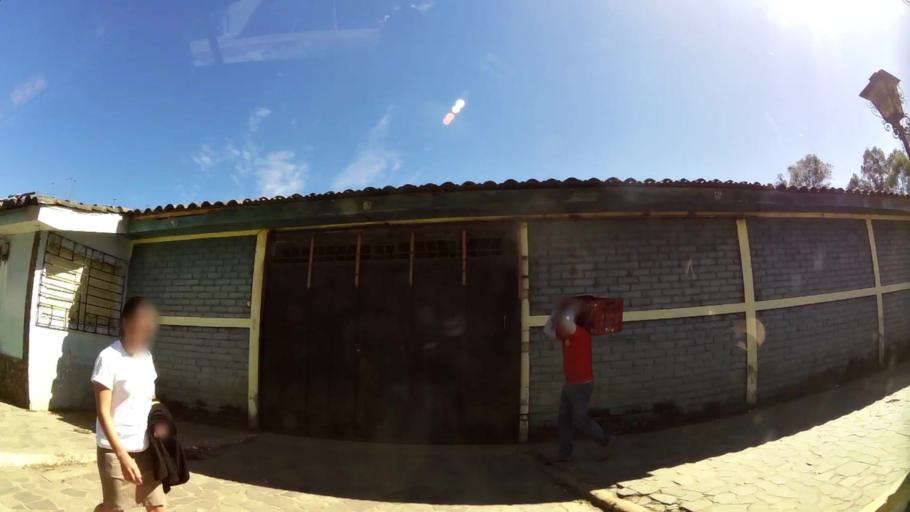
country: SV
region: Ahuachapan
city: Concepcion de Ataco
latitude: 13.8666
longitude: -89.8502
